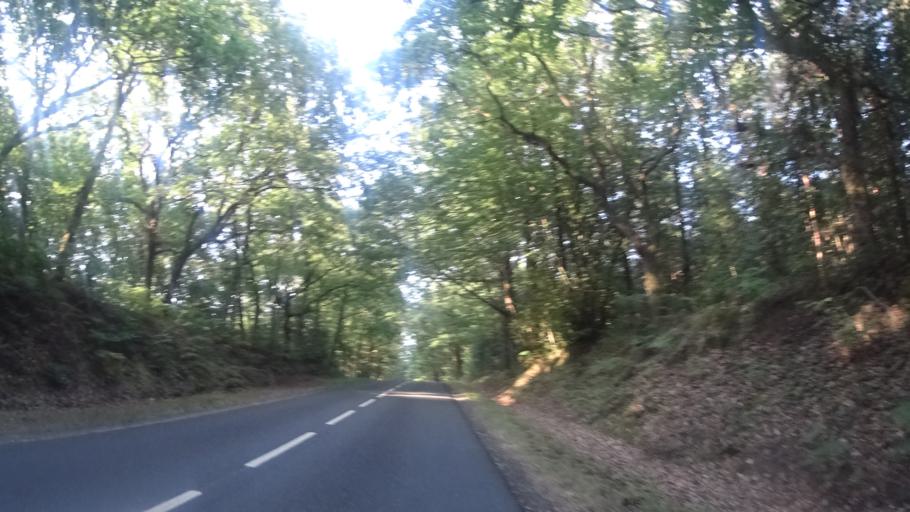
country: FR
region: Pays de la Loire
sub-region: Departement de la Loire-Atlantique
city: Saint-Mars-la-Jaille
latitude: 47.5468
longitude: -1.2304
